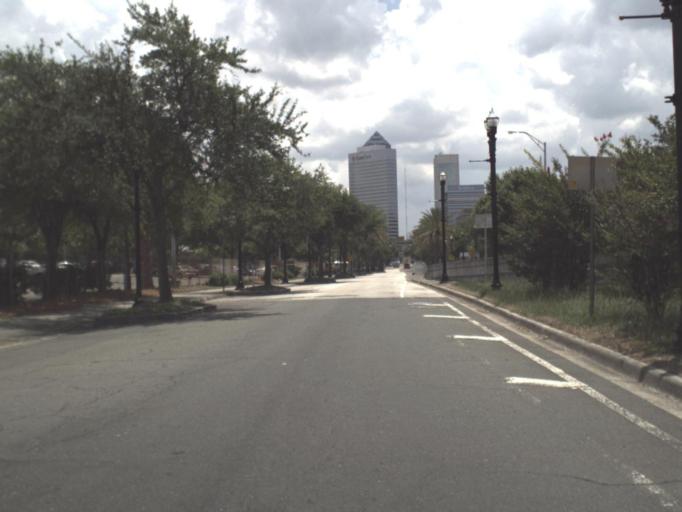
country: US
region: Florida
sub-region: Duval County
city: Jacksonville
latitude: 30.3299
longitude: -81.6741
